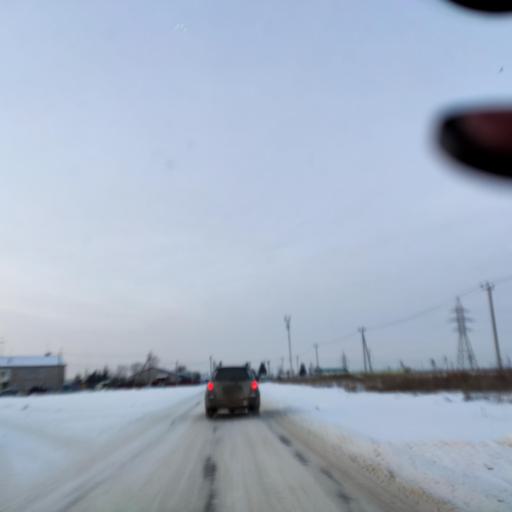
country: RU
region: Bashkortostan
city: Mikhaylovka
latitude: 54.8676
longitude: 55.7407
